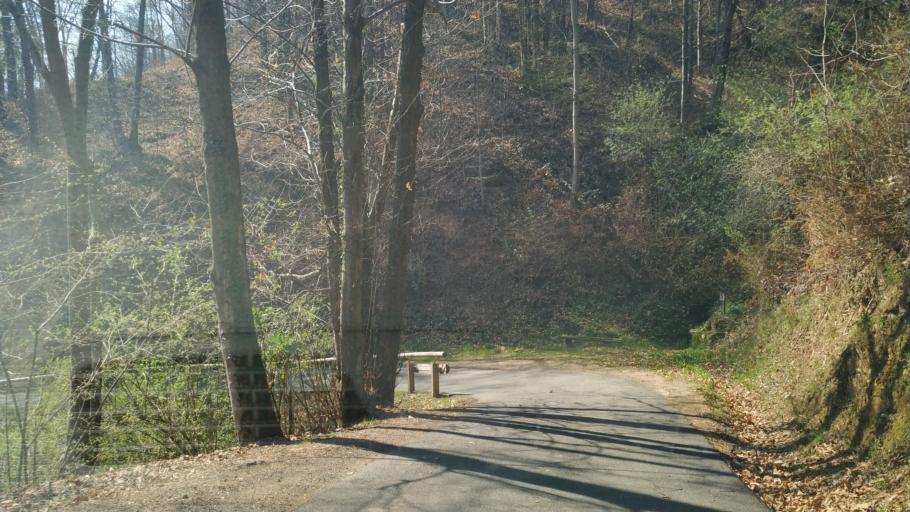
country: IT
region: Piedmont
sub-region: Provincia di Biella
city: Frazione Chiesa
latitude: 45.6895
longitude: 8.2007
